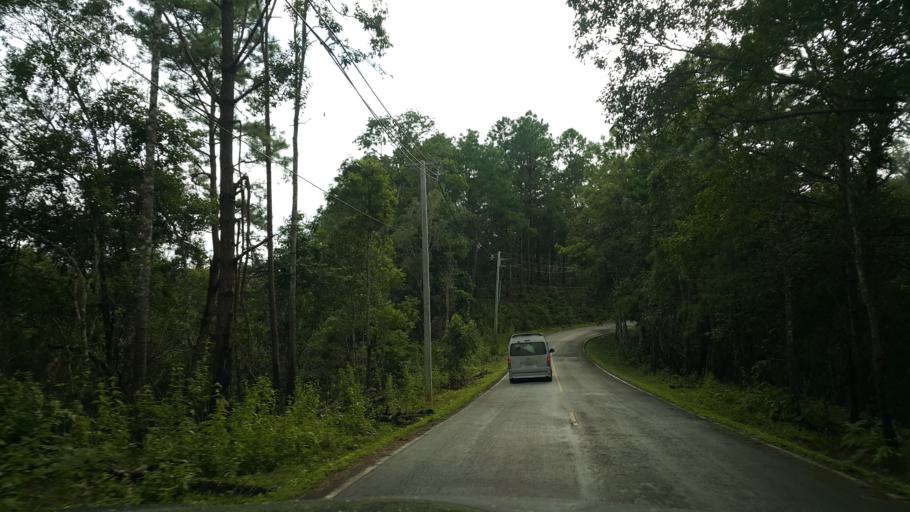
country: TH
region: Chiang Mai
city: Chaem Luang
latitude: 18.9152
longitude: 98.4896
